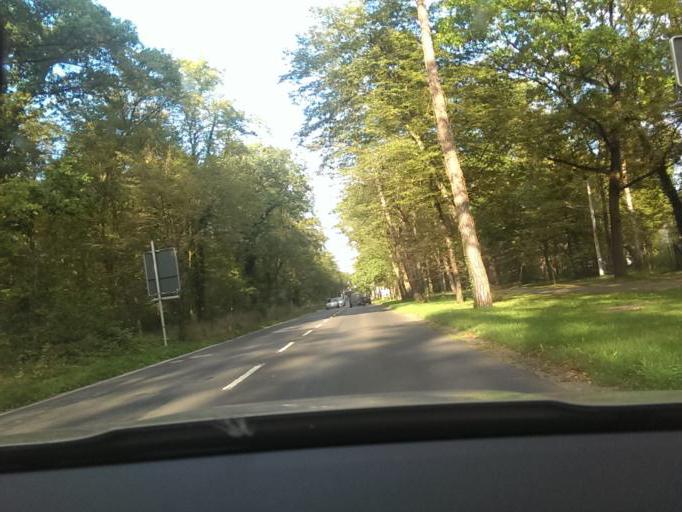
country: DE
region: Baden-Wuerttemberg
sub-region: Karlsruhe Region
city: Karlsruhe
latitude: 49.0233
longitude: 8.4207
